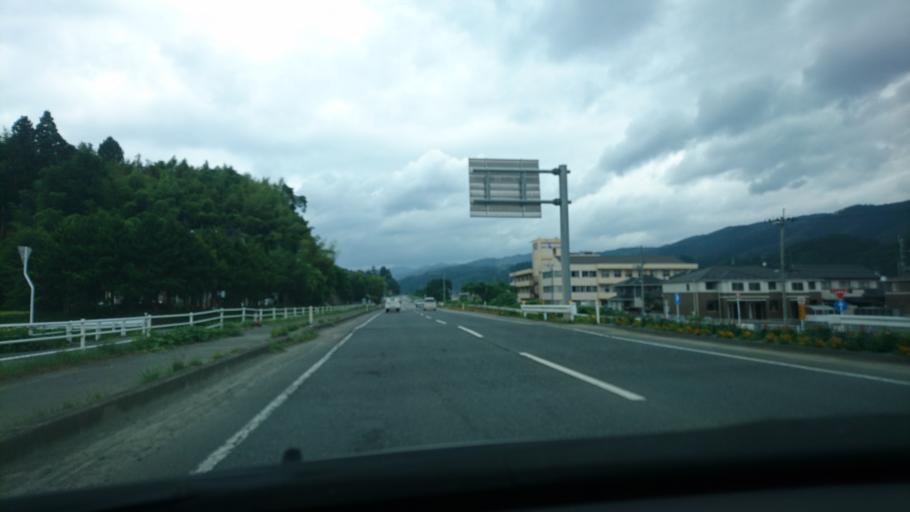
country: JP
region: Iwate
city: Ofunato
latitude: 38.9041
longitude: 141.5490
